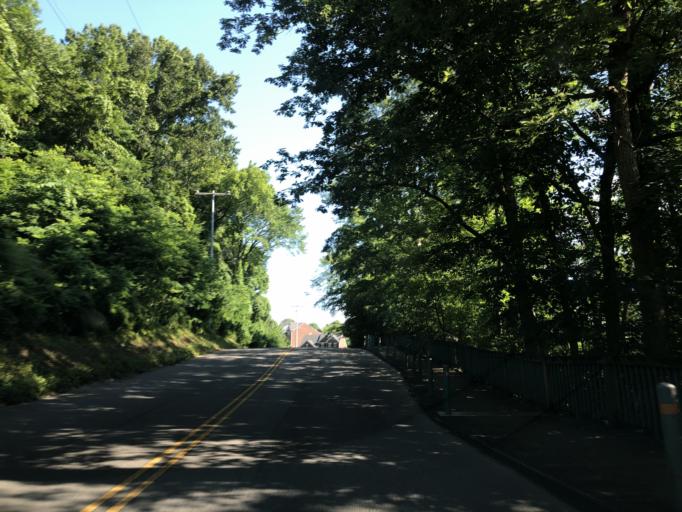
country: US
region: Tennessee
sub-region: Cheatham County
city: Pegram
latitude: 36.0654
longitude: -86.9551
